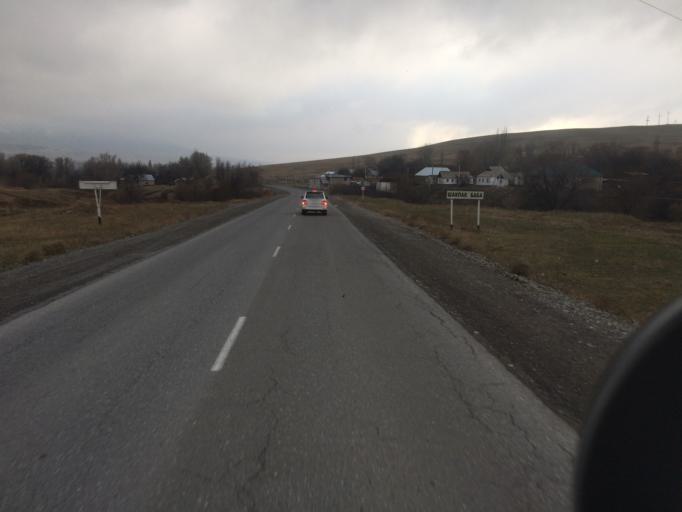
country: KZ
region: Ongtustik Qazaqstan
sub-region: Tulkibas Audany
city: Zhabagly
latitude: 42.5188
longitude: 70.5856
